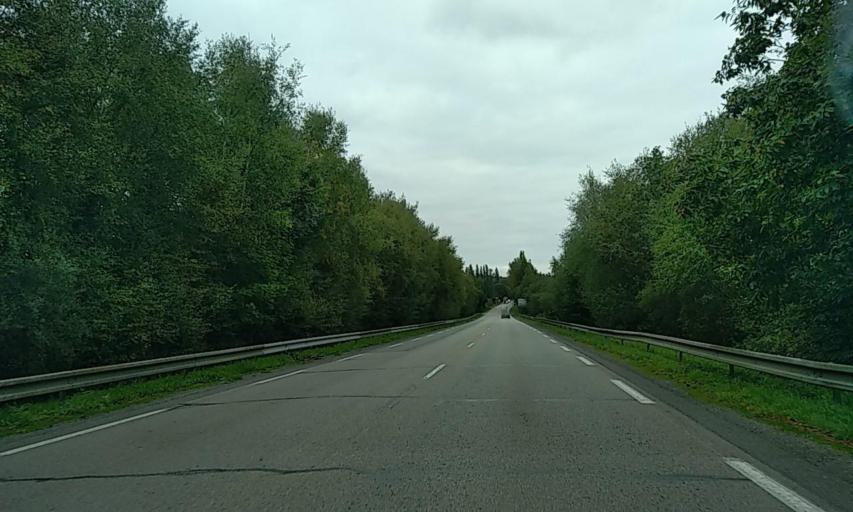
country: FR
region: Brittany
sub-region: Departement du Morbihan
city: Caudan
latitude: 47.8206
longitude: -3.3367
